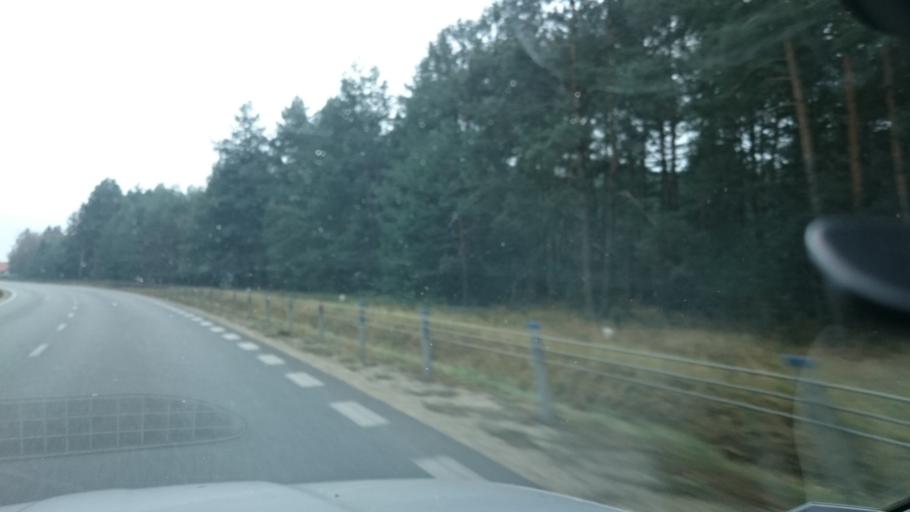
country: PL
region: Swietokrzyskie
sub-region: Powiat konecki
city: Konskie
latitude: 51.1511
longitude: 20.3617
